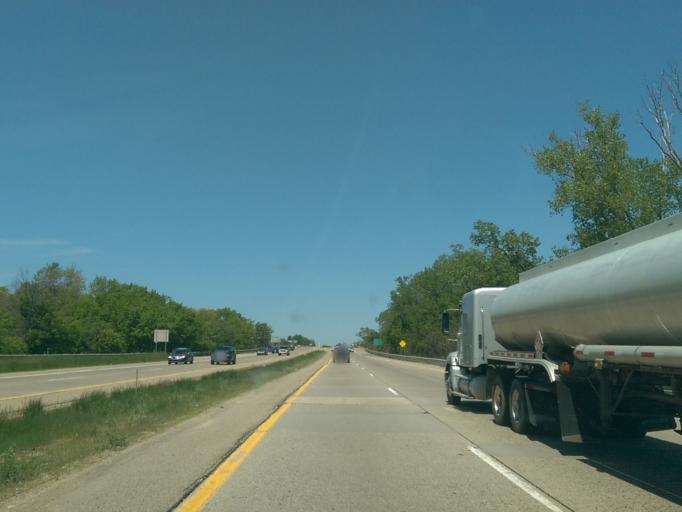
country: US
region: Michigan
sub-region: Ottawa County
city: Holland
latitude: 42.7988
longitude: -86.0824
